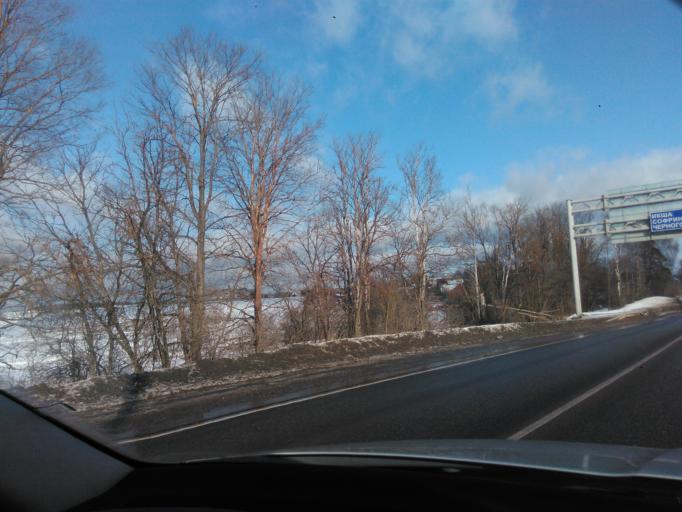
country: RU
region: Moskovskaya
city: Radumlya
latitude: 56.1042
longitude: 37.1844
